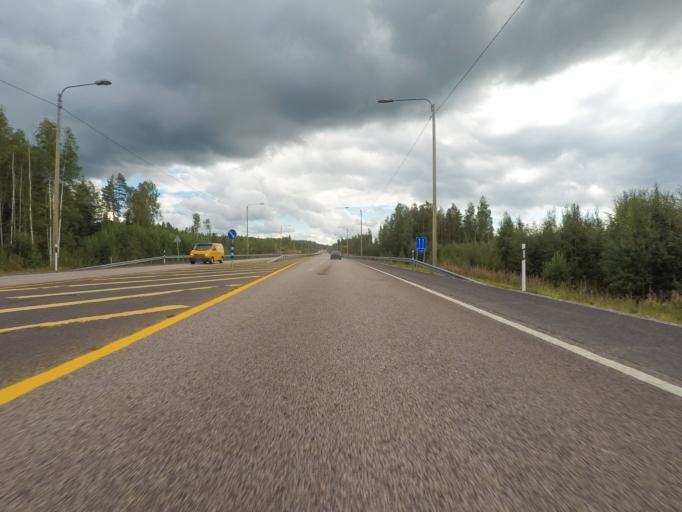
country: FI
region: Paijanne Tavastia
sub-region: Lahti
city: Hartola
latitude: 61.4259
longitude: 26.0154
